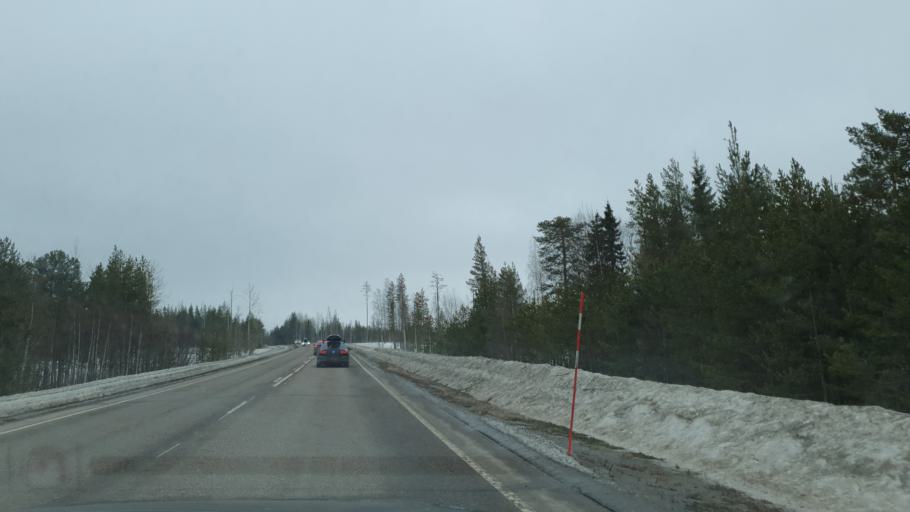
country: FI
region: Lapland
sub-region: Torniolaakso
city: Pello
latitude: 66.8448
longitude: 24.0299
